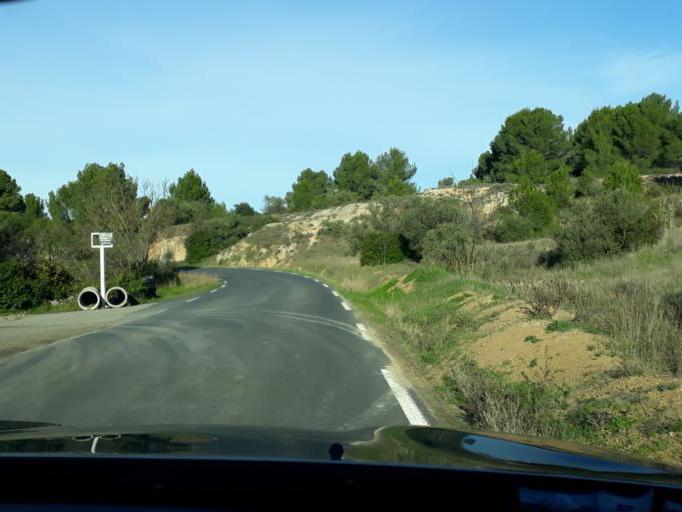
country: FR
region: Languedoc-Roussillon
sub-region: Departement de l'Herault
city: Castelnau-de-Guers
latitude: 43.4213
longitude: 3.4314
